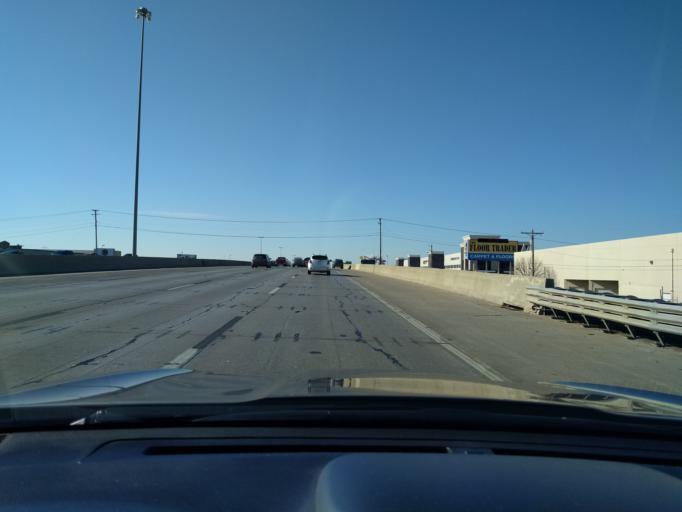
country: US
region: Oklahoma
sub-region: Oklahoma County
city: Oklahoma City
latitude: 35.4604
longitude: -97.5816
